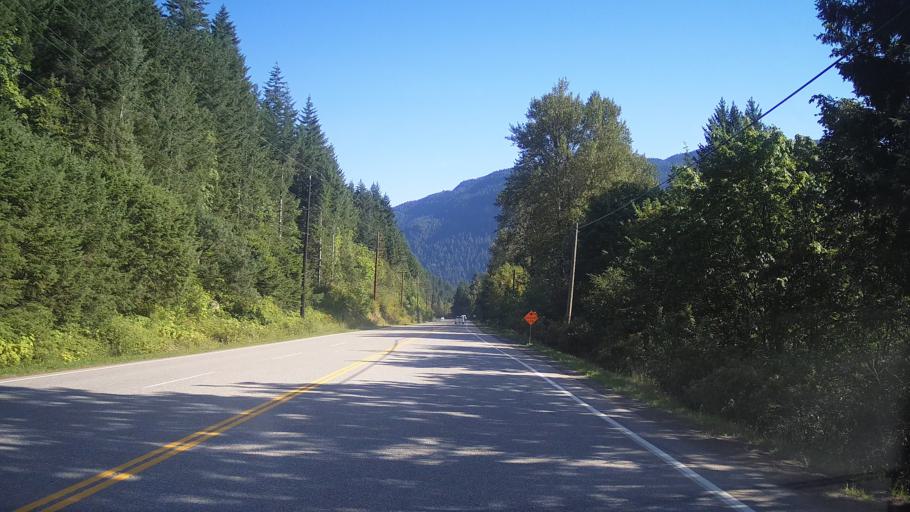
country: CA
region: British Columbia
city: Hope
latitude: 49.6808
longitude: -121.4172
